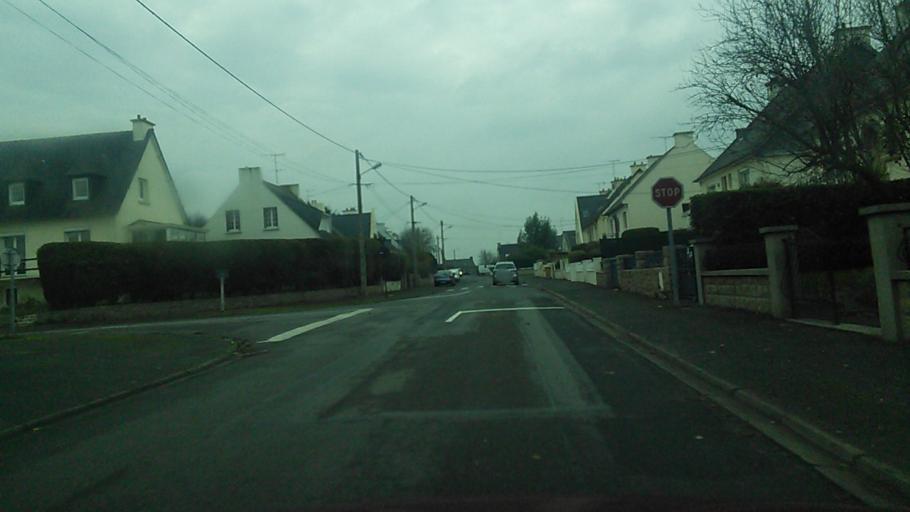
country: FR
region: Brittany
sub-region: Departement des Cotes-d'Armor
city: Pommeret
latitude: 48.4873
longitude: -2.6435
